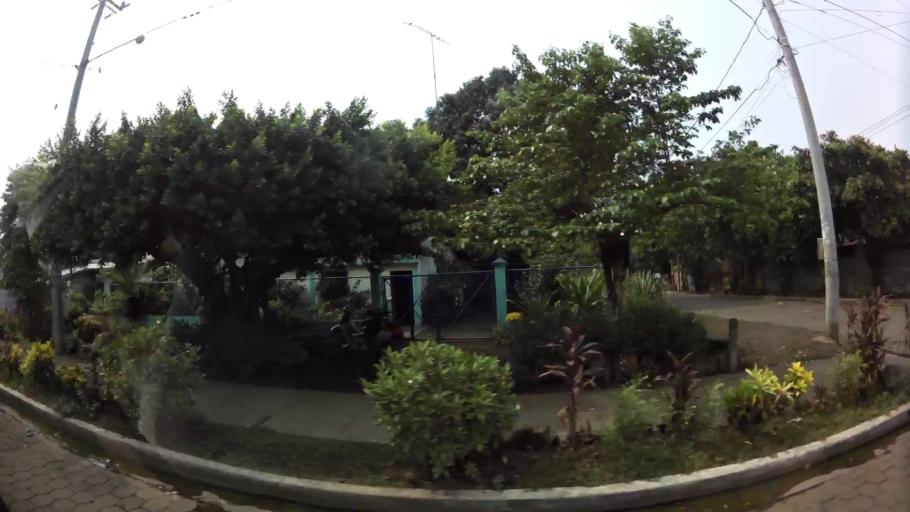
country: NI
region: Chinandega
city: Chinandega
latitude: 12.6281
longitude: -87.1414
